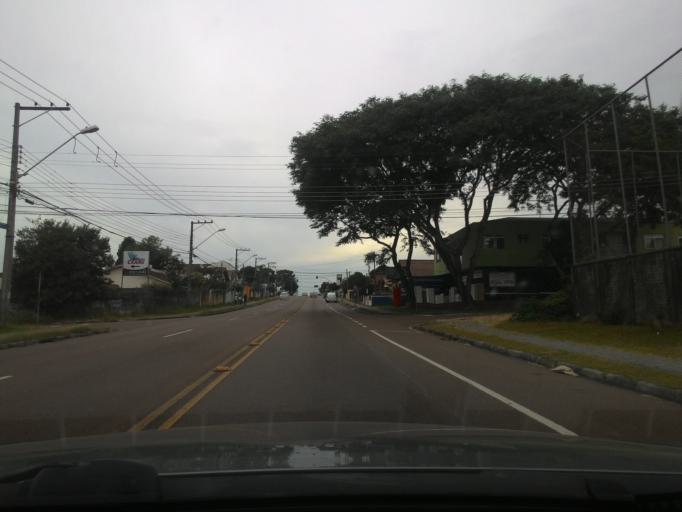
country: BR
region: Parana
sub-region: Pinhais
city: Pinhais
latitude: -25.4414
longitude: -49.2212
